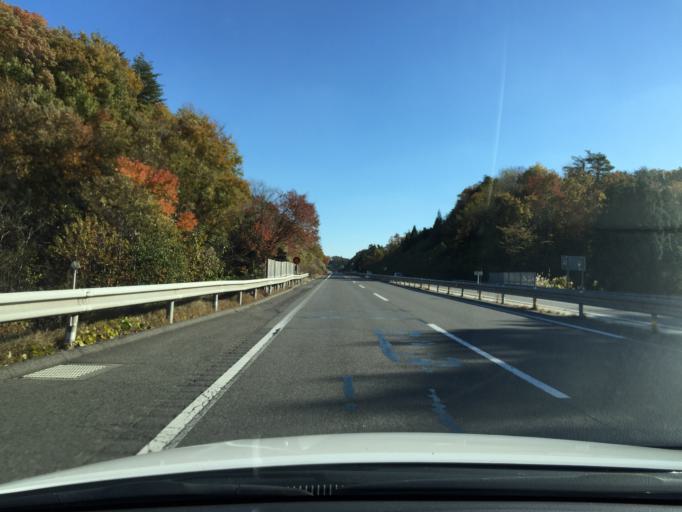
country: JP
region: Fukushima
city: Funehikimachi-funehiki
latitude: 37.4082
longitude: 140.5669
